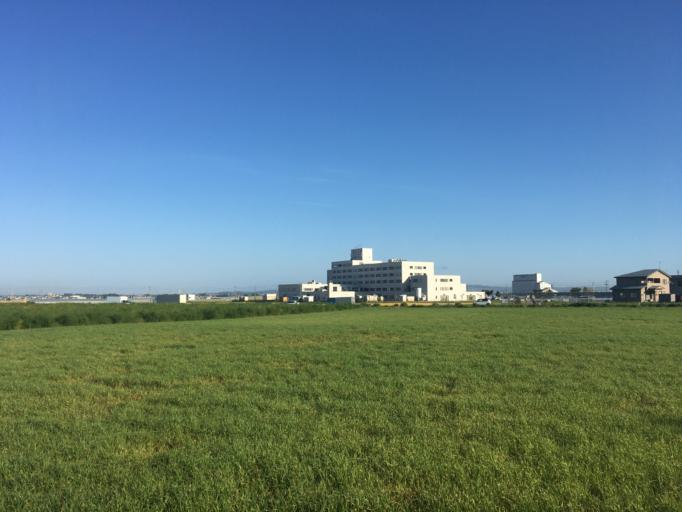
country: JP
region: Aomori
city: Kuroishi
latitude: 40.6510
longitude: 140.5788
